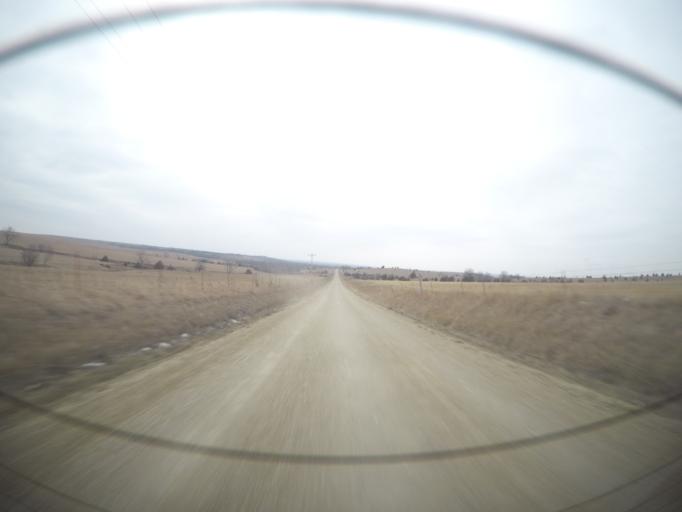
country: US
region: Kansas
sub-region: Pottawatomie County
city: Wamego
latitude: 39.1518
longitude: -96.2662
